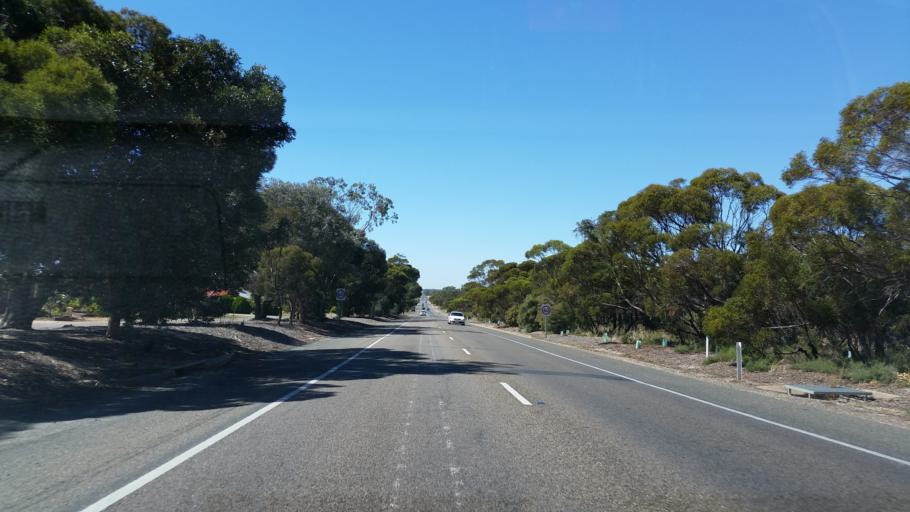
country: AU
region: South Australia
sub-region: Murray Bridge
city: Murray Bridge
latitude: -35.1341
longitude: 139.2386
